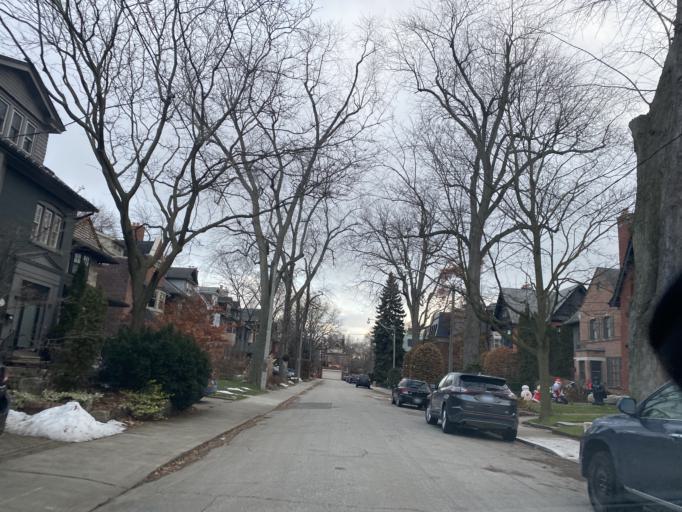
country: CA
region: Ontario
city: Toronto
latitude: 43.6761
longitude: -79.3706
